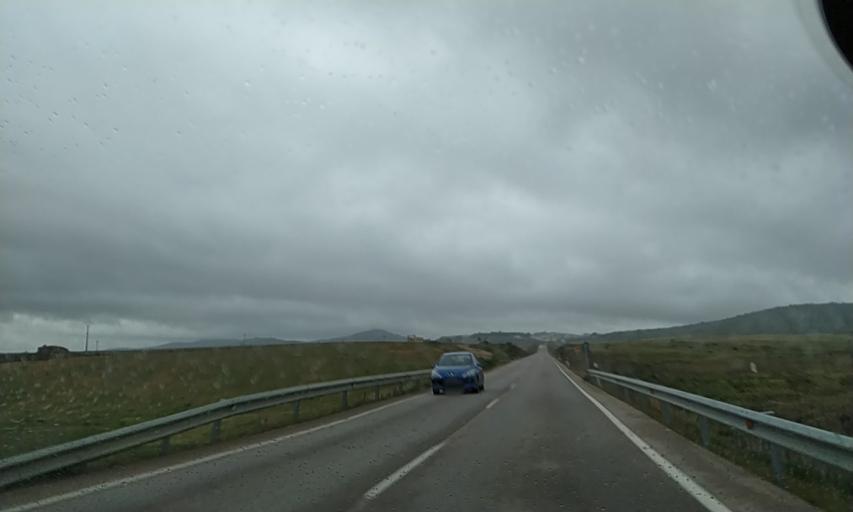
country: ES
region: Extremadura
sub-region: Provincia de Caceres
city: Caceres
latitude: 39.5081
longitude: -6.3924
